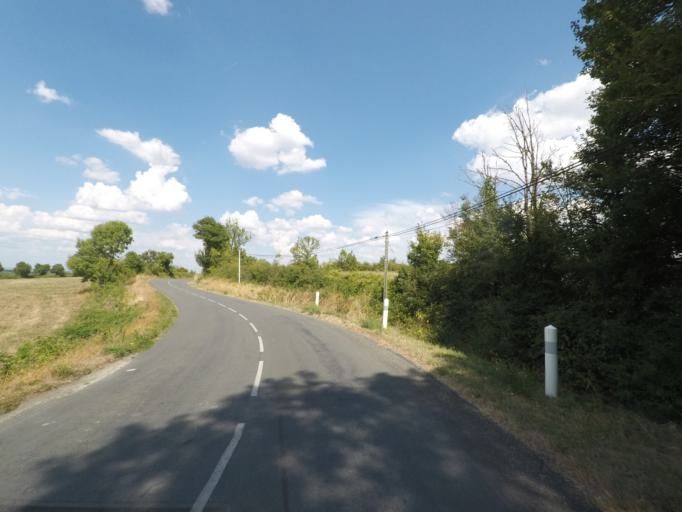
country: FR
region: Midi-Pyrenees
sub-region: Departement du Lot
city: Le Vigan
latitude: 44.6525
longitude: 1.5778
